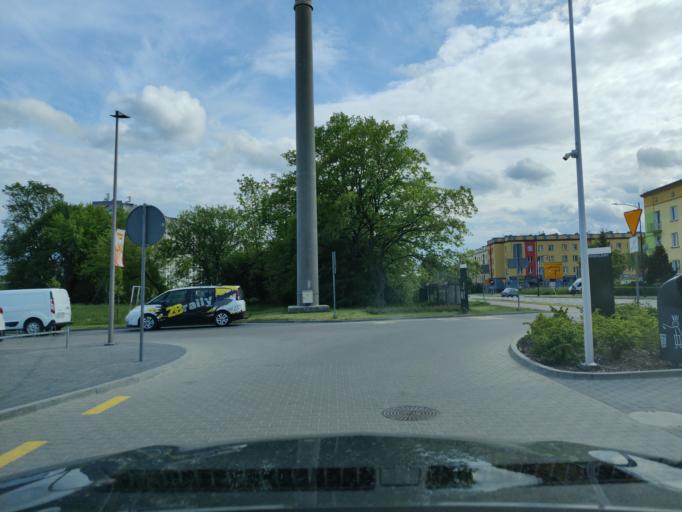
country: PL
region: Swietokrzyskie
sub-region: Powiat skarzyski
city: Skarzysko-Kamienna
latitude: 51.1176
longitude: 20.8622
